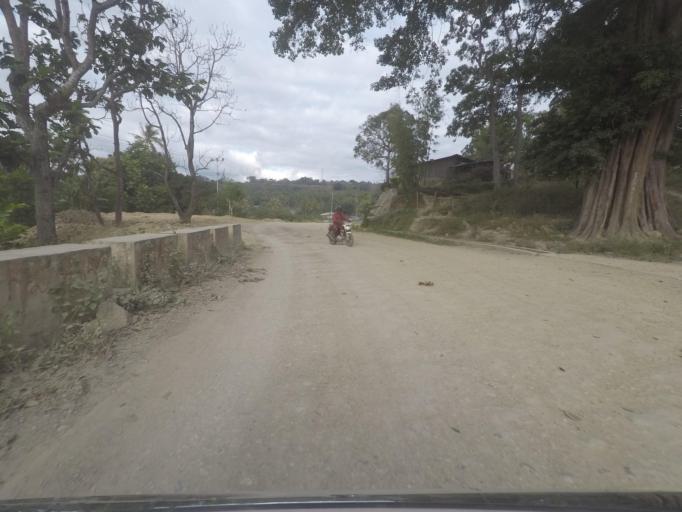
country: TL
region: Baucau
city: Venilale
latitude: -8.5922
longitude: 126.3867
